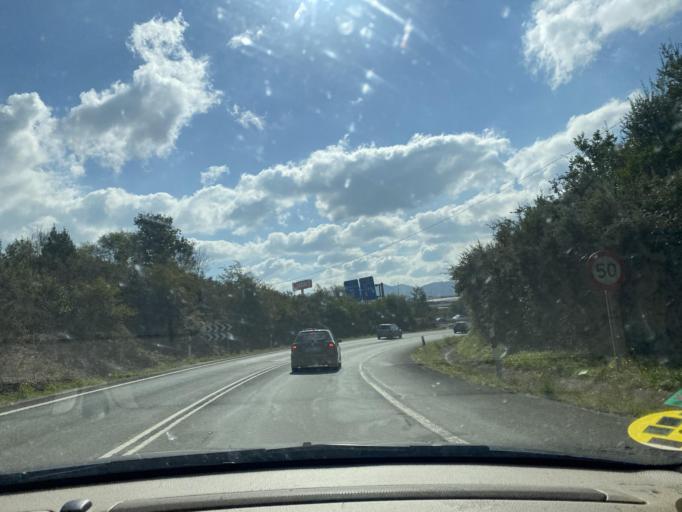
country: ES
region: Asturias
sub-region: Province of Asturias
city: Lugones
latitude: 43.3935
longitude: -5.8049
